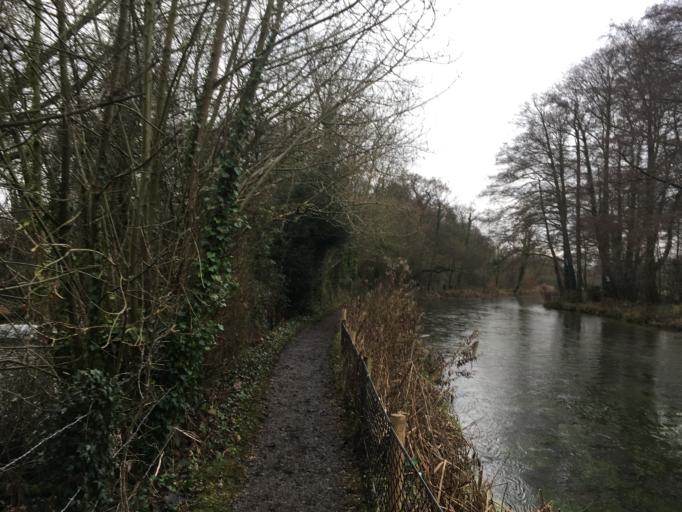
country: GB
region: England
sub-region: Hampshire
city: Compton
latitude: 50.9975
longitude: -1.3360
